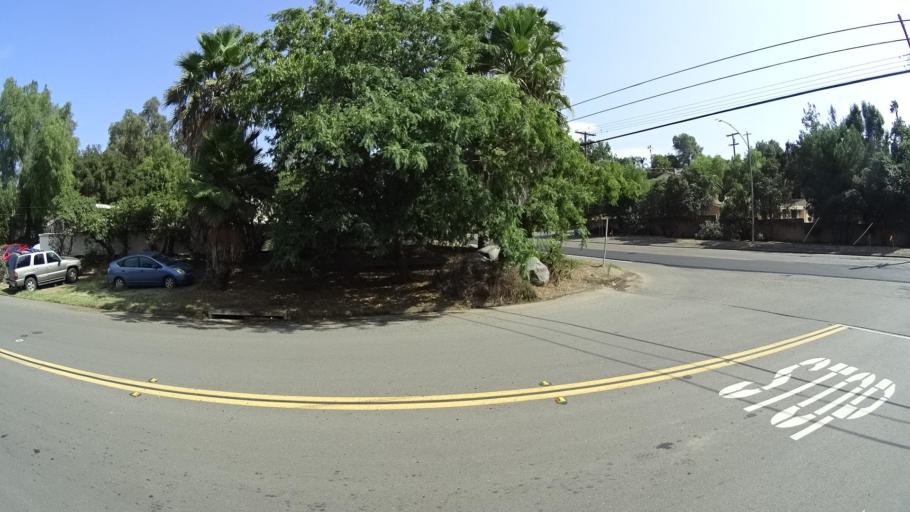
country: US
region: California
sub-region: San Diego County
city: Escondido
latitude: 33.1092
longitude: -117.0486
